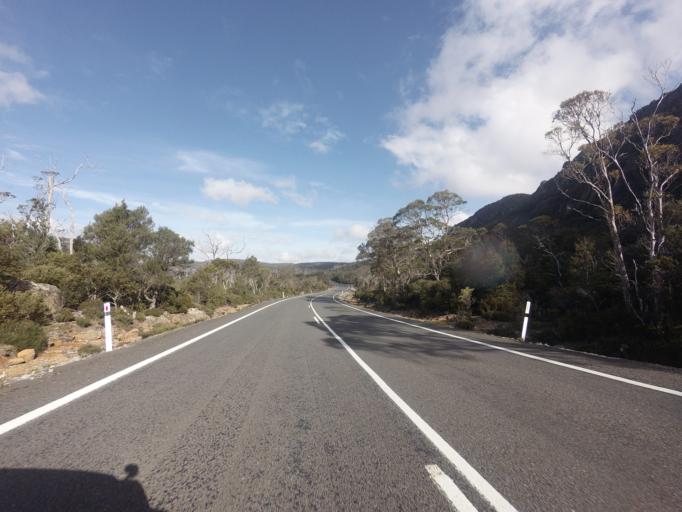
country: AU
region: Tasmania
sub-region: Meander Valley
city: Deloraine
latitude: -41.7215
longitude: 146.7246
